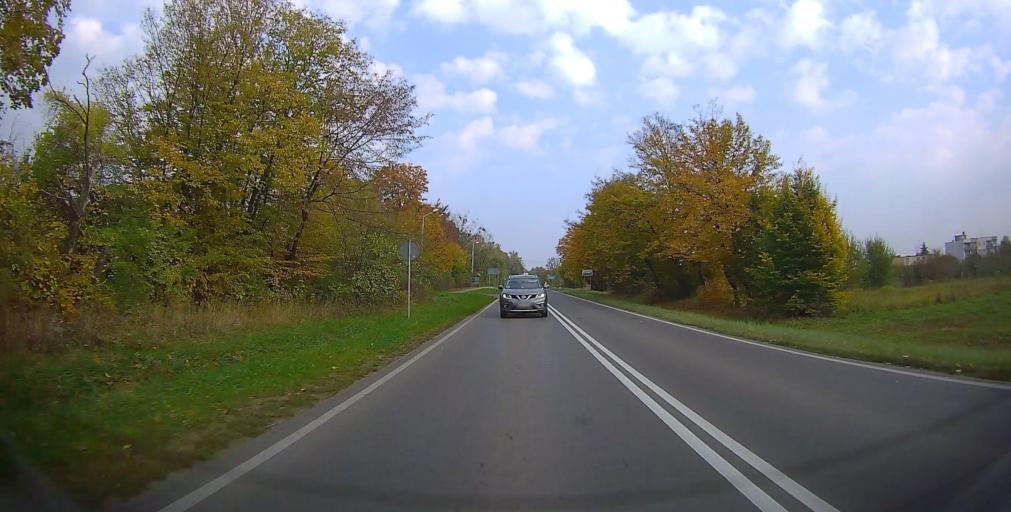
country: PL
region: Masovian Voivodeship
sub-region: Powiat grojecki
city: Belsk Duzy
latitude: 51.8111
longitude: 20.7951
